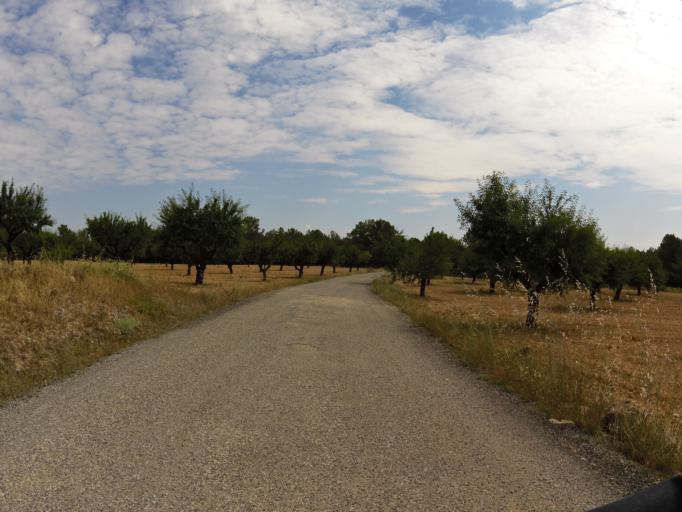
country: ES
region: Castille-La Mancha
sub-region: Provincia de Albacete
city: Casas Ibanez
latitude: 39.3561
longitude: -1.4737
